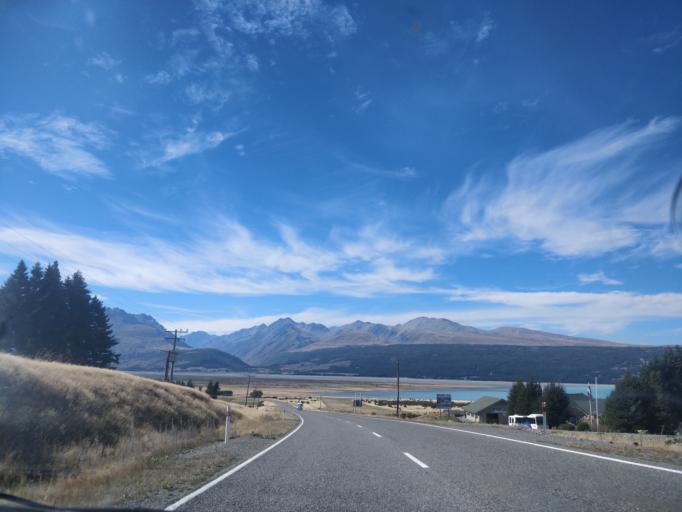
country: NZ
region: Canterbury
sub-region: Timaru District
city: Pleasant Point
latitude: -43.9124
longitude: 170.1196
